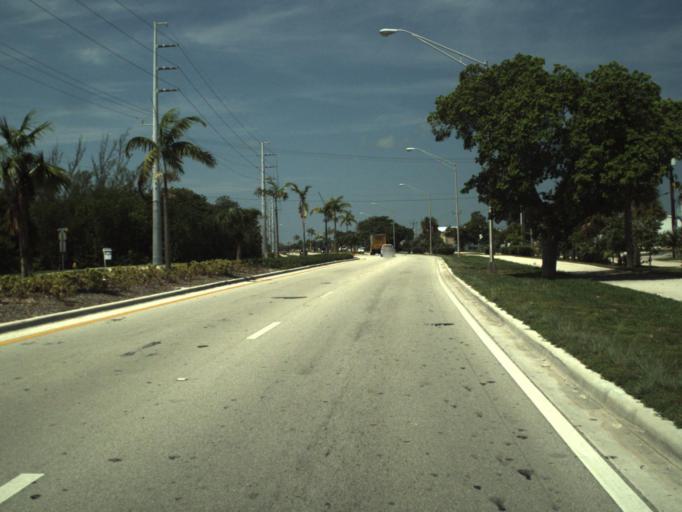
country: US
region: Florida
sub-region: Monroe County
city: Marathon
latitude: 24.7281
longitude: -81.0408
